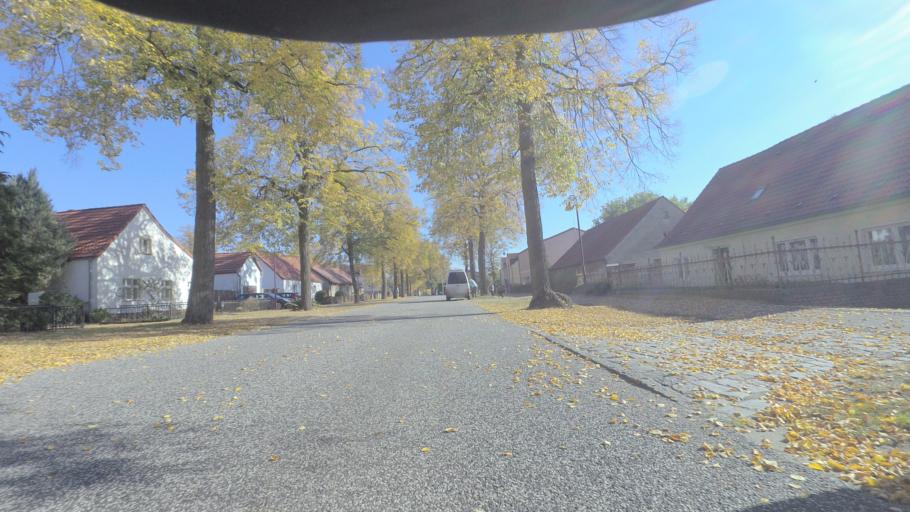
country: DE
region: Brandenburg
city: Mittenwalde
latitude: 52.2449
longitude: 13.4945
